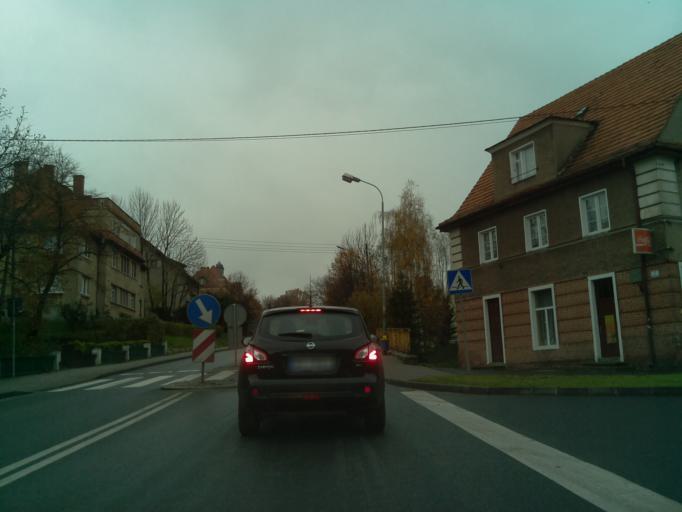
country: PL
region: Lower Silesian Voivodeship
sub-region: Powiat jaworski
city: Bolkow
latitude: 50.9243
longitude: 16.1038
